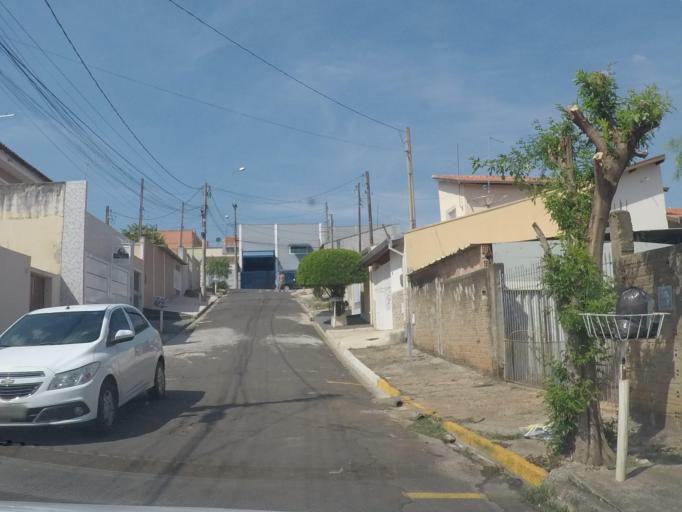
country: BR
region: Sao Paulo
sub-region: Sumare
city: Sumare
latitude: -22.8164
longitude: -47.2590
